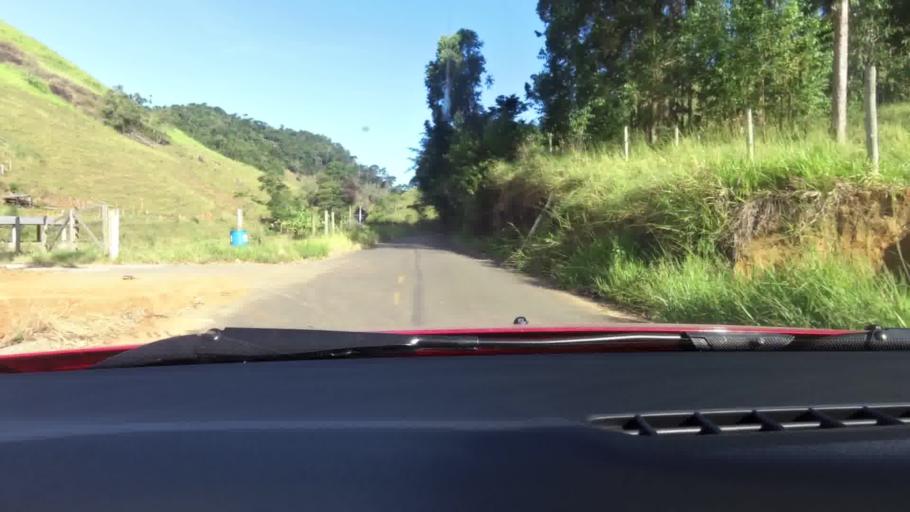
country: BR
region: Espirito Santo
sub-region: Guarapari
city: Guarapari
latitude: -20.5511
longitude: -40.5566
